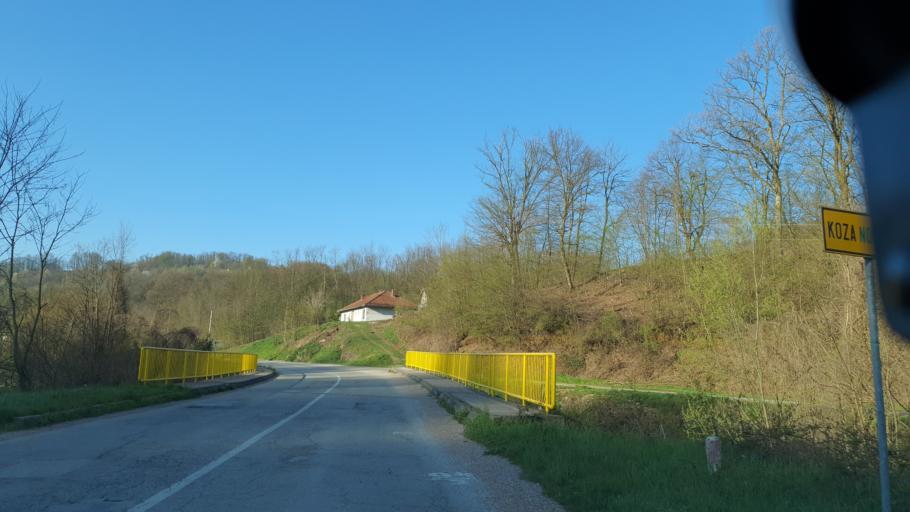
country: RS
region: Central Serbia
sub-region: Kolubarski Okrug
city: Osecina
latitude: 44.3179
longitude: 19.5265
